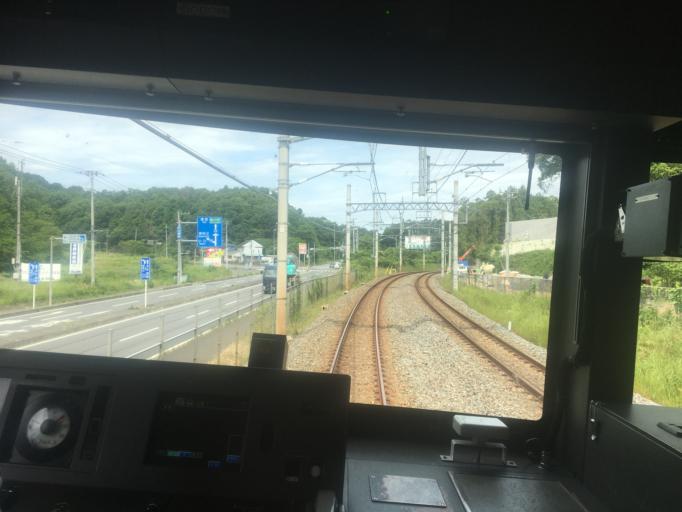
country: JP
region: Saitama
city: Ogawa
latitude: 36.0519
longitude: 139.3054
